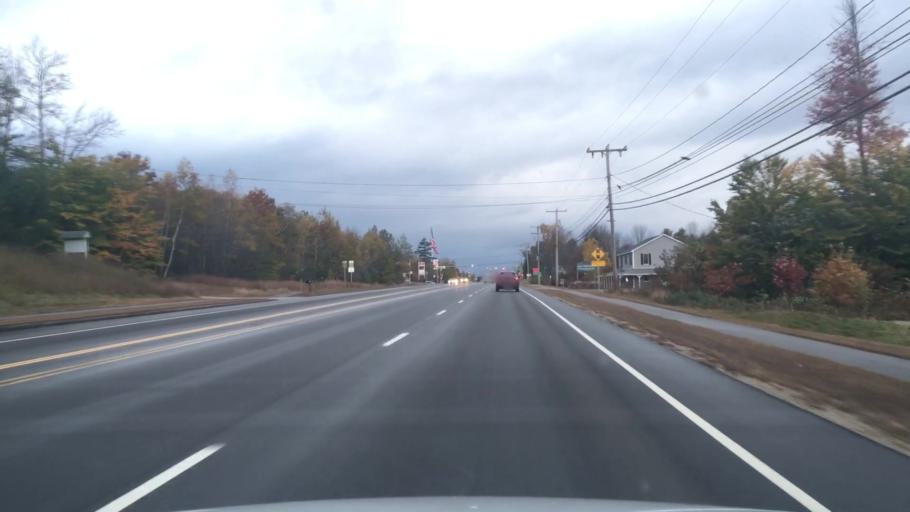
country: US
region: New Hampshire
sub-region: Merrimack County
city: Chichester
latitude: 43.2424
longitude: -71.4009
